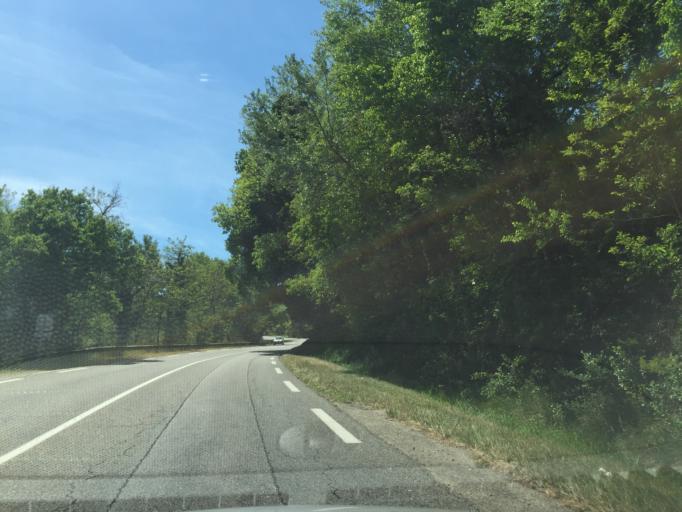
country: FR
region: Provence-Alpes-Cote d'Azur
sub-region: Departement du Var
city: Villecroze
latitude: 43.5478
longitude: 6.3093
